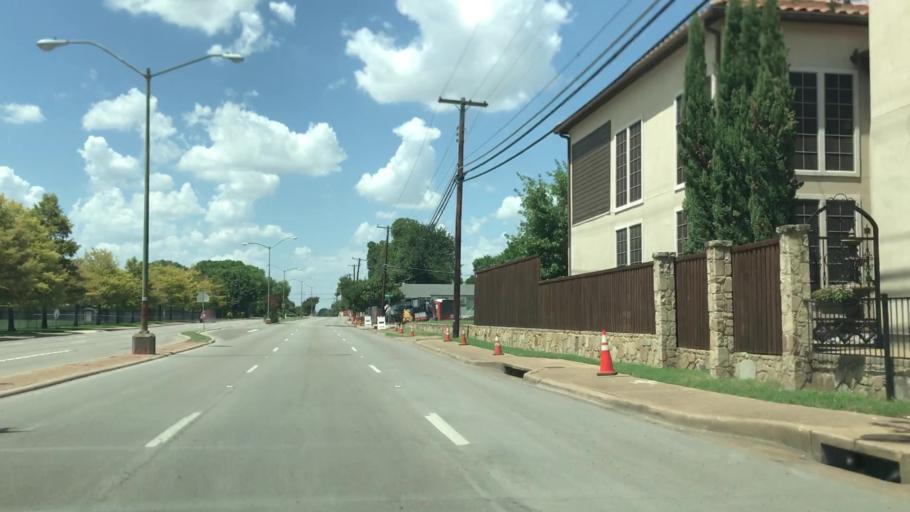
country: US
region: Texas
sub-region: Dallas County
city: University Park
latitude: 32.8879
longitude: -96.8384
